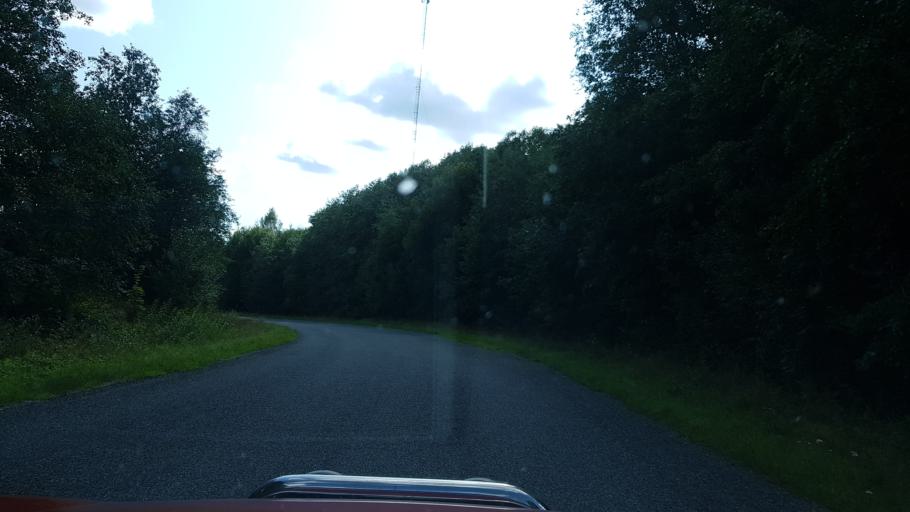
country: LV
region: Aluksnes Rajons
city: Aluksne
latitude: 57.5941
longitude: 27.0858
